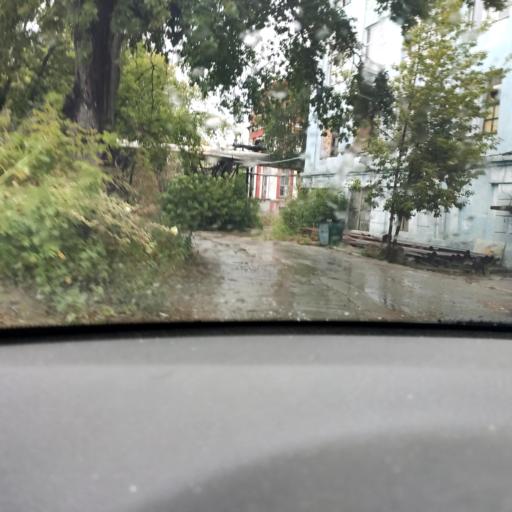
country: RU
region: Samara
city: Samara
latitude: 53.2222
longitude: 50.1474
